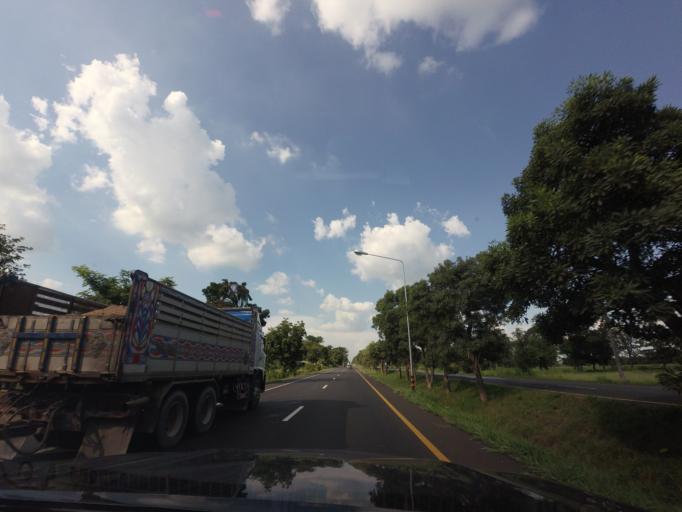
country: TH
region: Nakhon Ratchasima
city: Bua Lai
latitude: 15.7069
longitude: 102.5864
